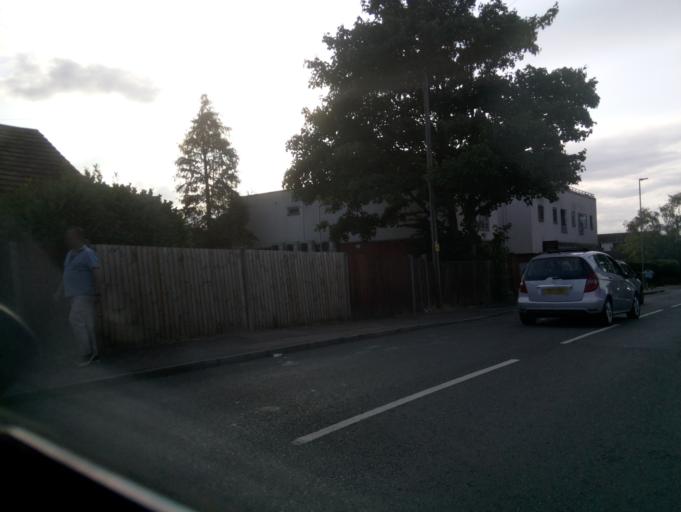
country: GB
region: England
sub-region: Gloucestershire
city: Barnwood
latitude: 51.8425
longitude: -2.2179
